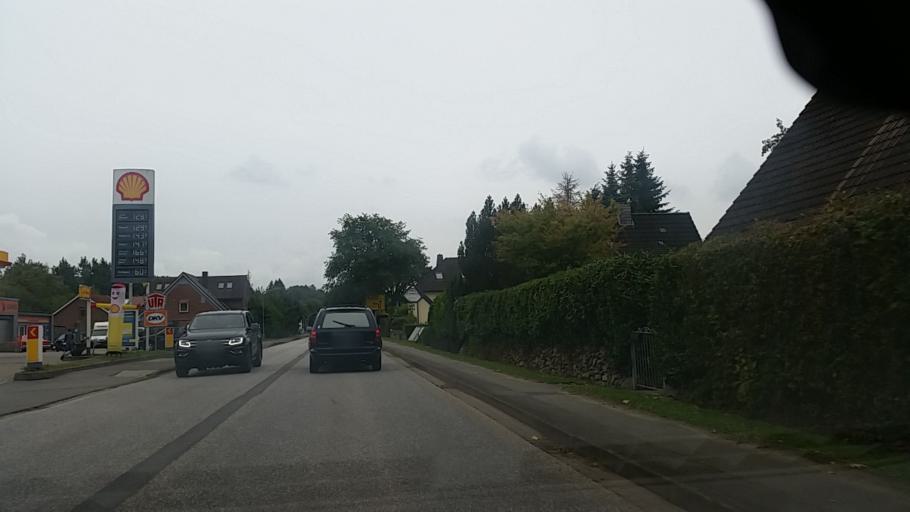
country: DE
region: Schleswig-Holstein
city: Kayhude
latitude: 53.7533
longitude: 10.1278
